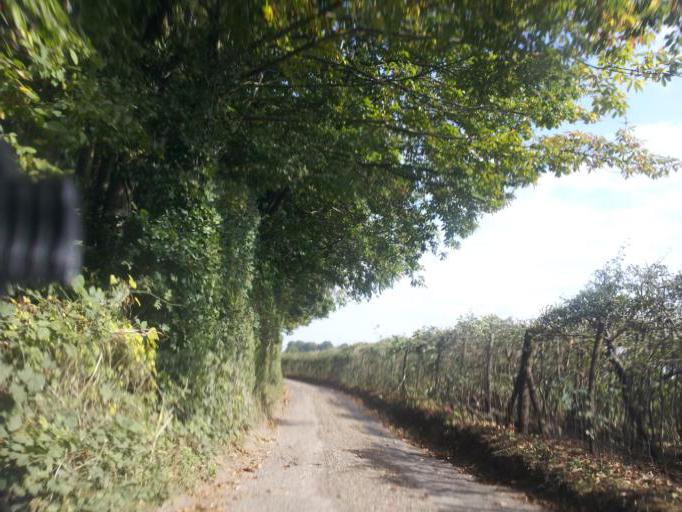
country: GB
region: England
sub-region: Kent
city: Boxley
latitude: 51.3223
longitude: 0.5318
